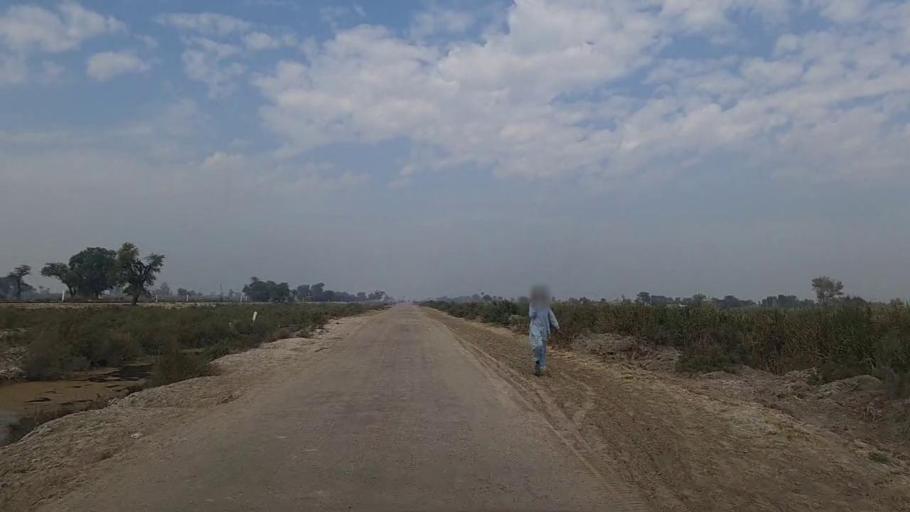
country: PK
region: Sindh
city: Daur
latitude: 26.3763
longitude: 68.3565
